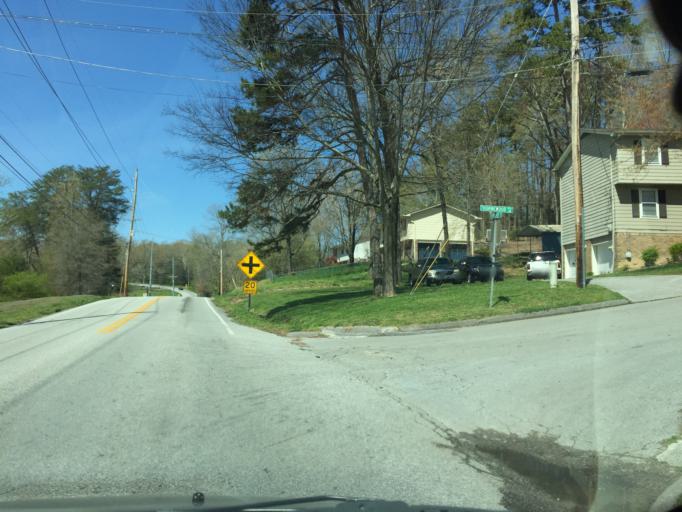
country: US
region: Tennessee
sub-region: Hamilton County
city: Middle Valley
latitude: 35.2015
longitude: -85.2060
